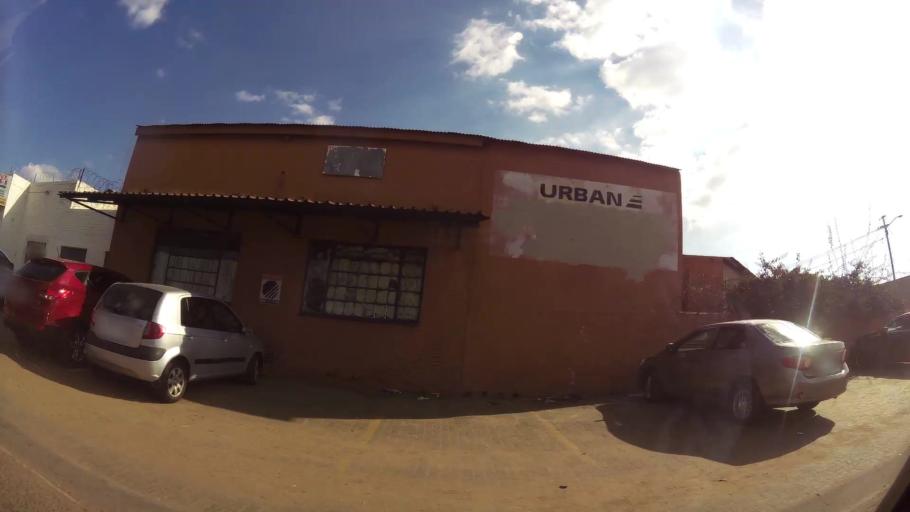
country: ZA
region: Gauteng
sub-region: Ekurhuleni Metropolitan Municipality
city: Germiston
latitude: -26.1973
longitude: 28.1513
